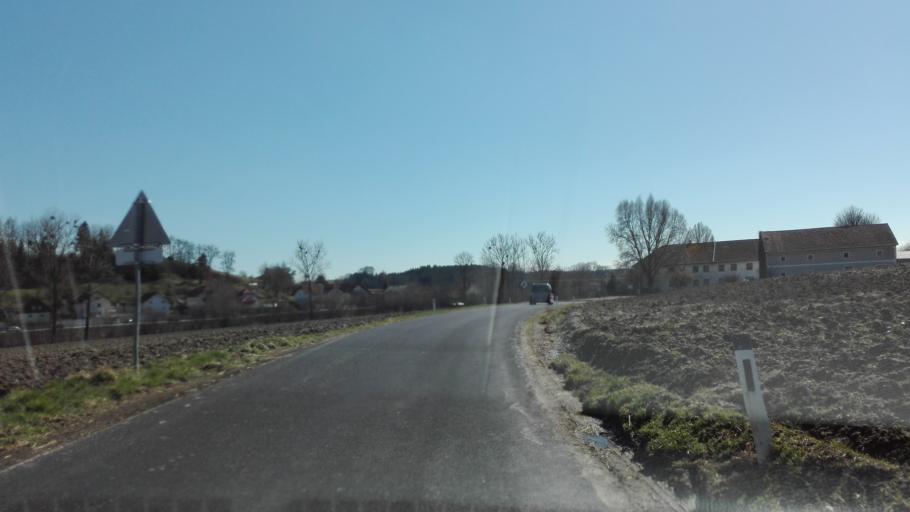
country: AT
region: Upper Austria
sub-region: Wels-Land
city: Buchkirchen
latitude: 48.2186
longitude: 13.9707
